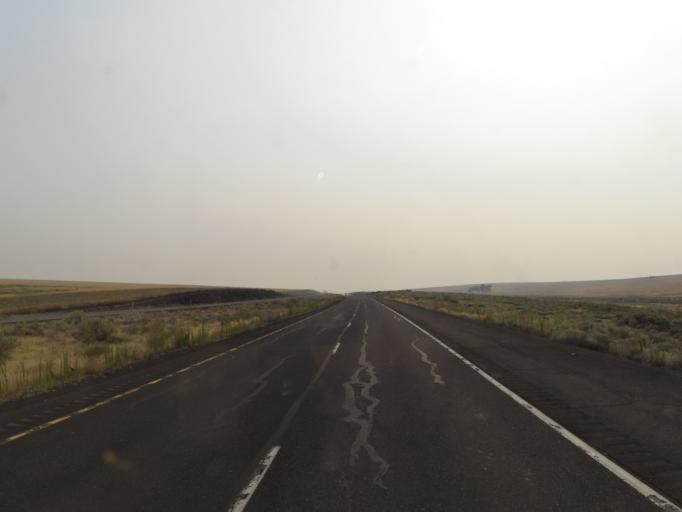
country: US
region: Washington
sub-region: Franklin County
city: Connell
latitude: 46.8127
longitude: -118.7127
